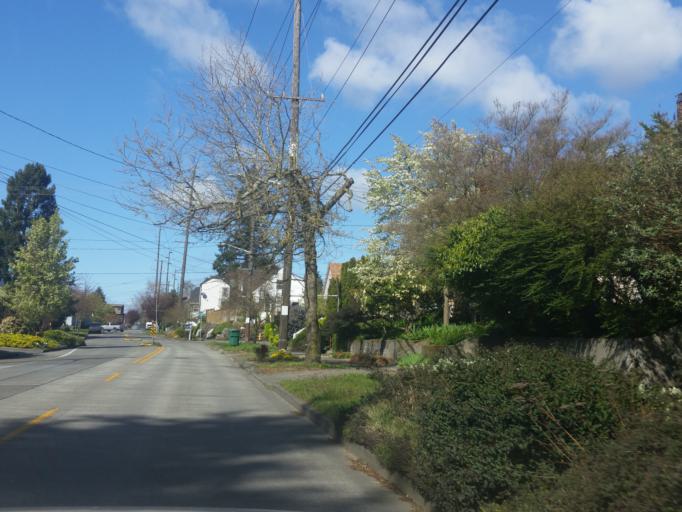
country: US
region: Washington
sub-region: King County
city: Shoreline
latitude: 47.6812
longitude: -122.3605
